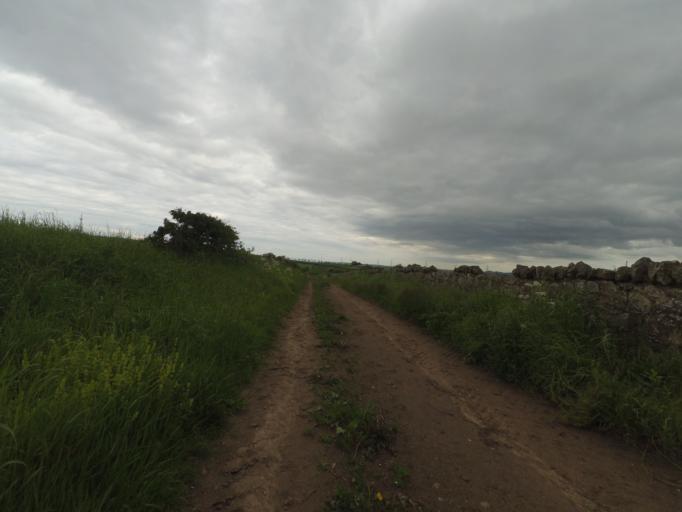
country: GB
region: Scotland
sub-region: East Lothian
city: Prestonpans
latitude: 55.9249
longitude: -2.9897
